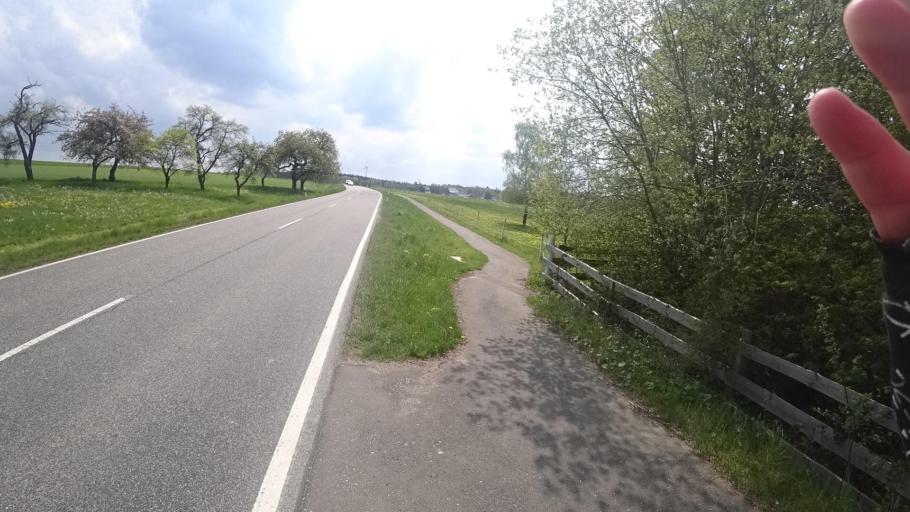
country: DE
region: Rheinland-Pfalz
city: Braunshorn
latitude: 50.0776
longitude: 7.5153
